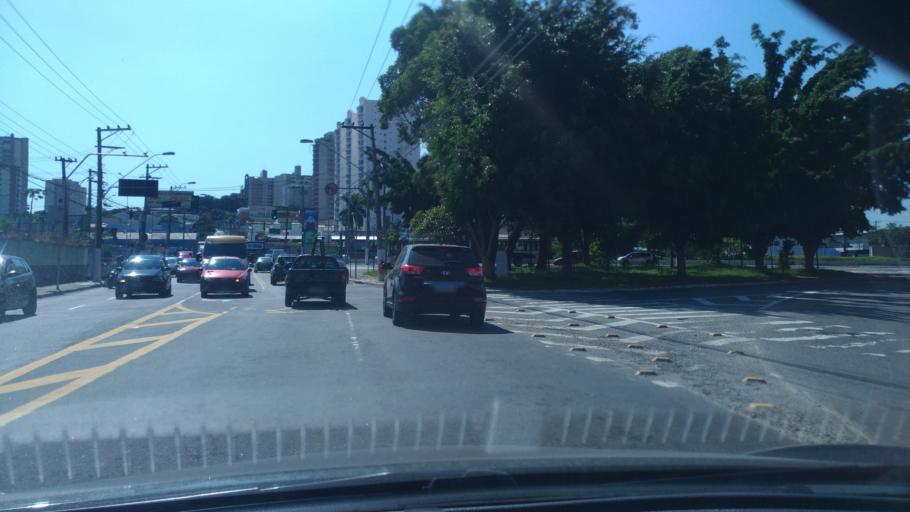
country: BR
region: Sao Paulo
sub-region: Santo Andre
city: Santo Andre
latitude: -23.6693
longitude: -46.5543
